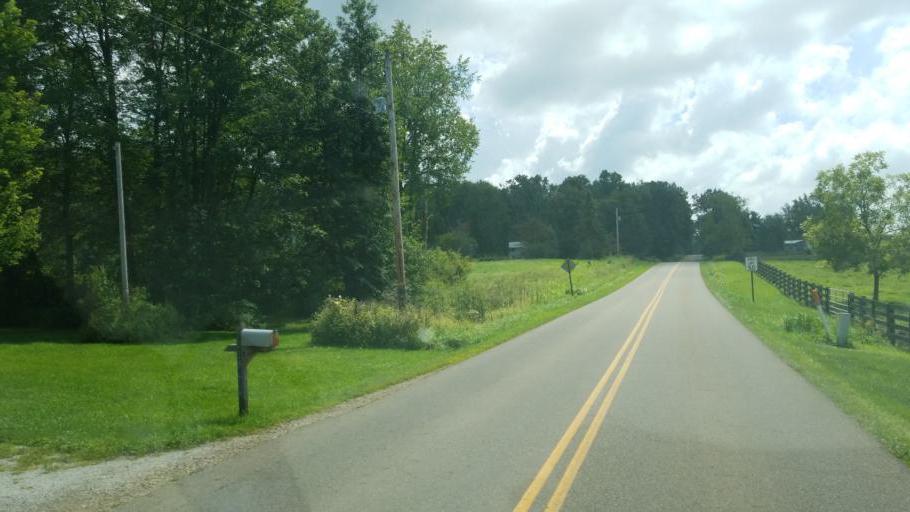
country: US
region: Ohio
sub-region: Knox County
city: Mount Vernon
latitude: 40.4486
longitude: -82.4871
